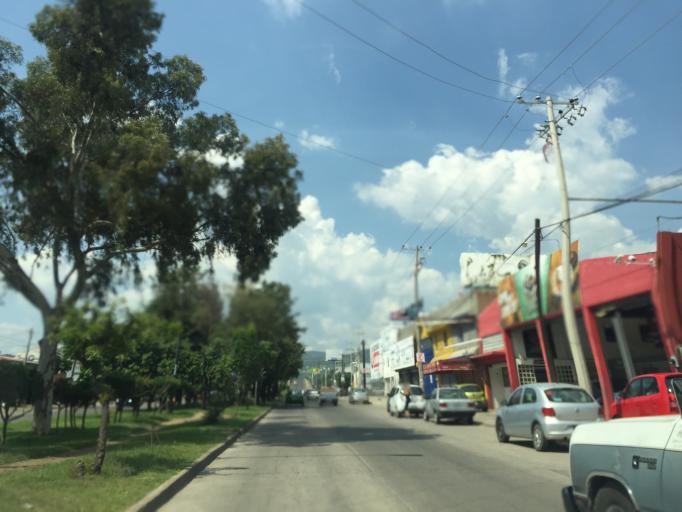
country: MX
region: Guanajuato
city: Leon
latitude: 21.1696
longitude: -101.6641
